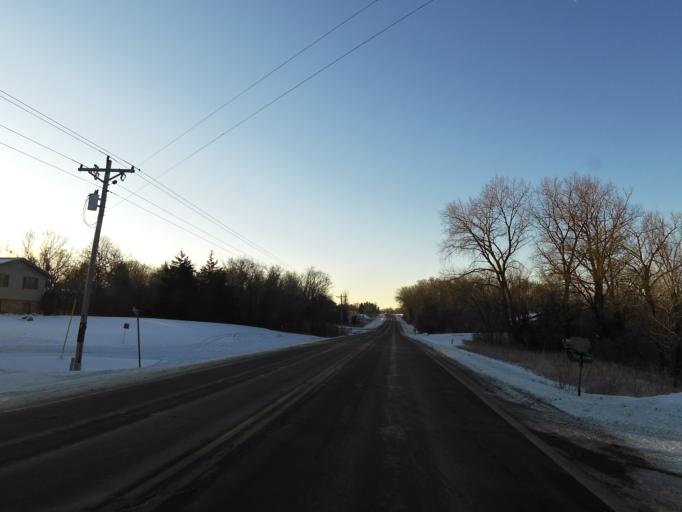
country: US
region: Minnesota
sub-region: Scott County
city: Prior Lake
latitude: 44.7136
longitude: -93.3791
